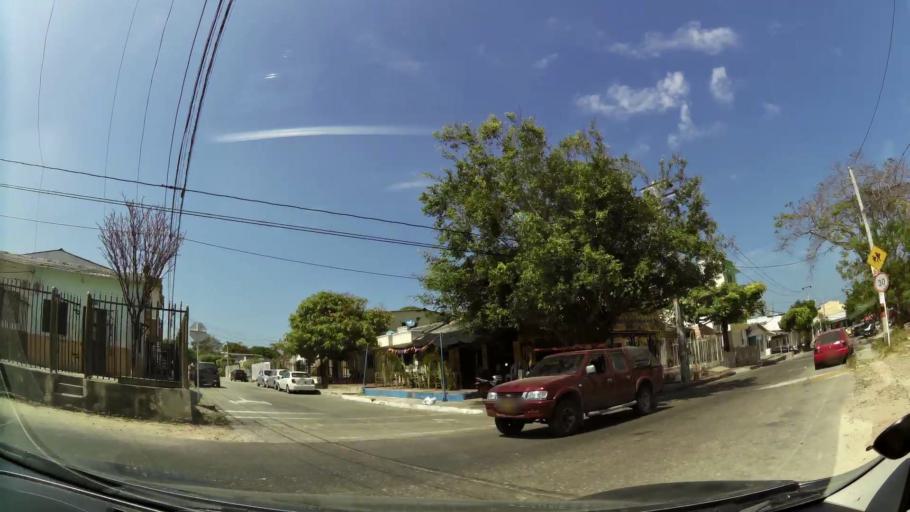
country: CO
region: Atlantico
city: Barranquilla
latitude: 10.9676
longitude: -74.8057
